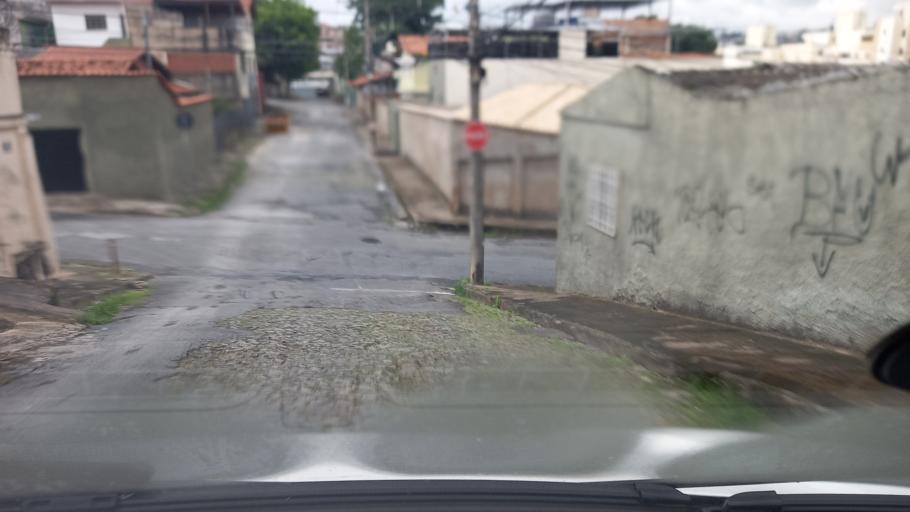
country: BR
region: Minas Gerais
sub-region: Contagem
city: Contagem
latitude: -19.9112
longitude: -43.9994
